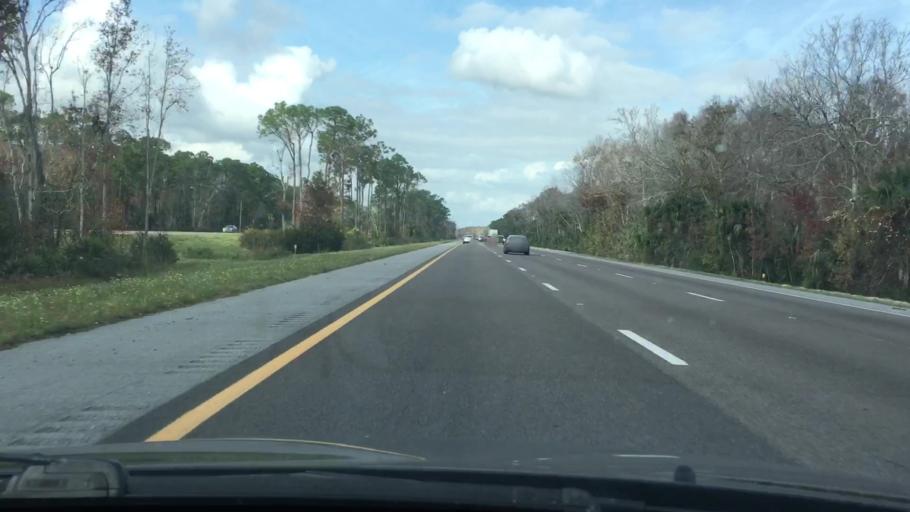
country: US
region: Florida
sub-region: Volusia County
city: Edgewater
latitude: 28.9134
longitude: -80.9350
